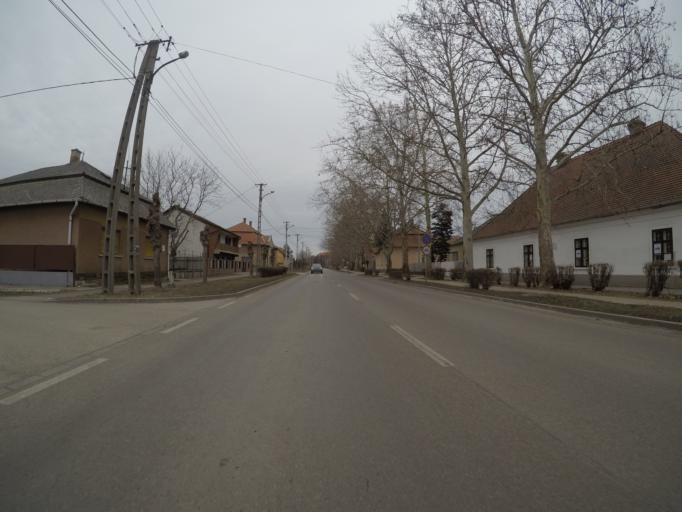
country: HU
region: Jasz-Nagykun-Szolnok
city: Jaszapati
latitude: 47.5154
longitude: 20.1438
